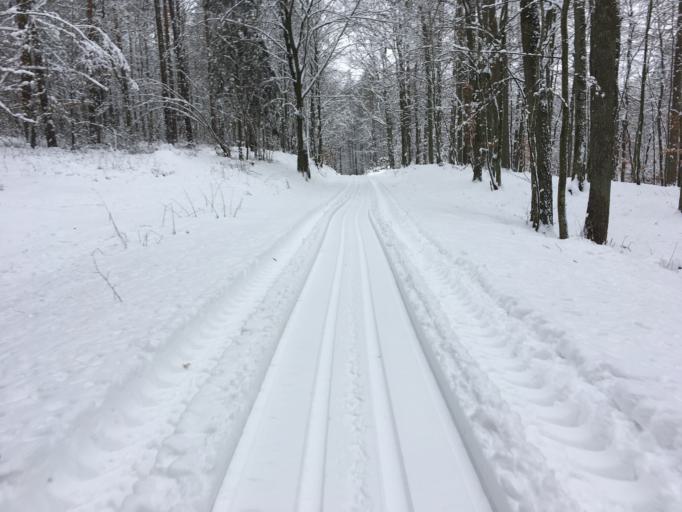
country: PL
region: Kujawsko-Pomorskie
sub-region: Powiat brodnicki
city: Gorzno
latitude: 53.1894
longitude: 19.6869
